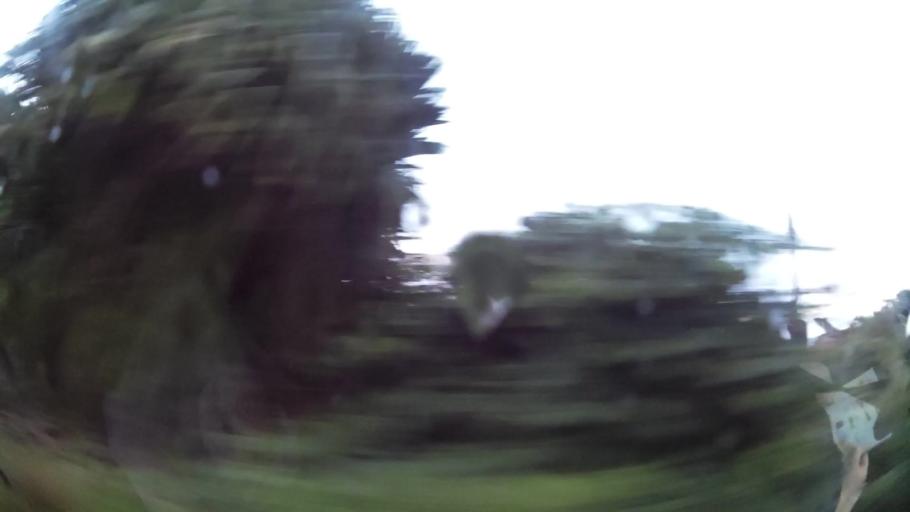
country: DM
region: Saint Andrew
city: Marigot
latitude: 15.5519
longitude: -61.2956
